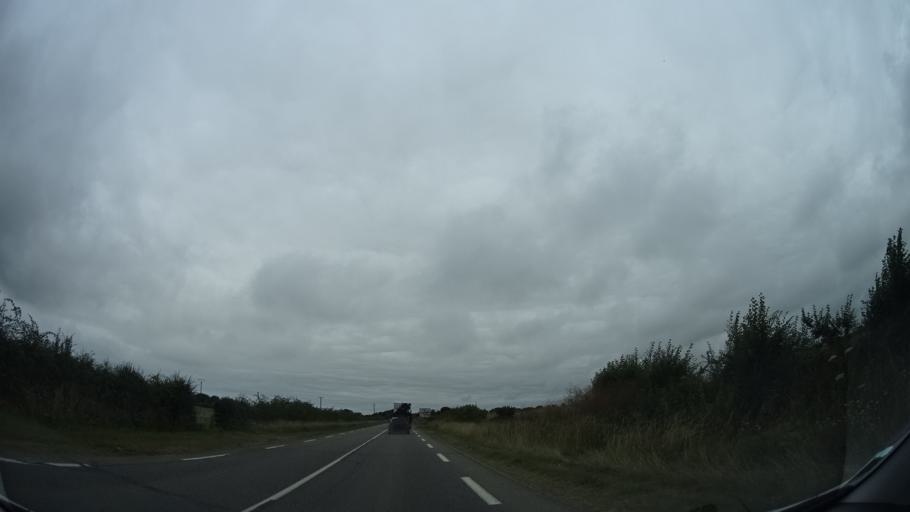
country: FR
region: Lower Normandy
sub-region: Departement de la Manche
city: Portbail
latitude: 49.3607
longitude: -1.6919
